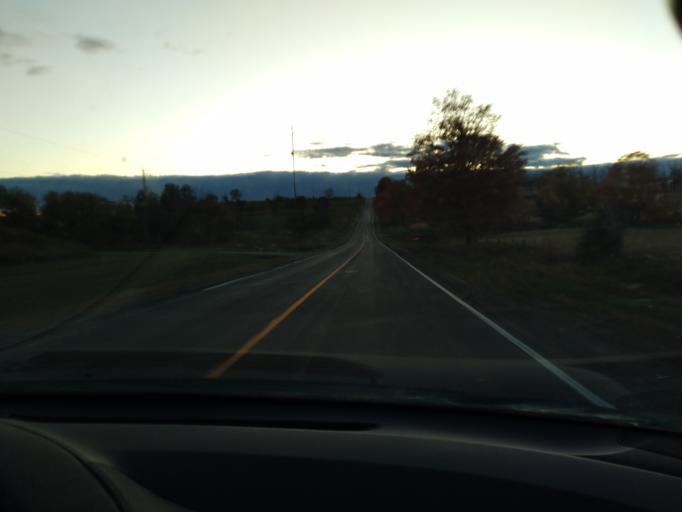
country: CA
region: Ontario
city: Innisfil
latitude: 44.2400
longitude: -79.6534
